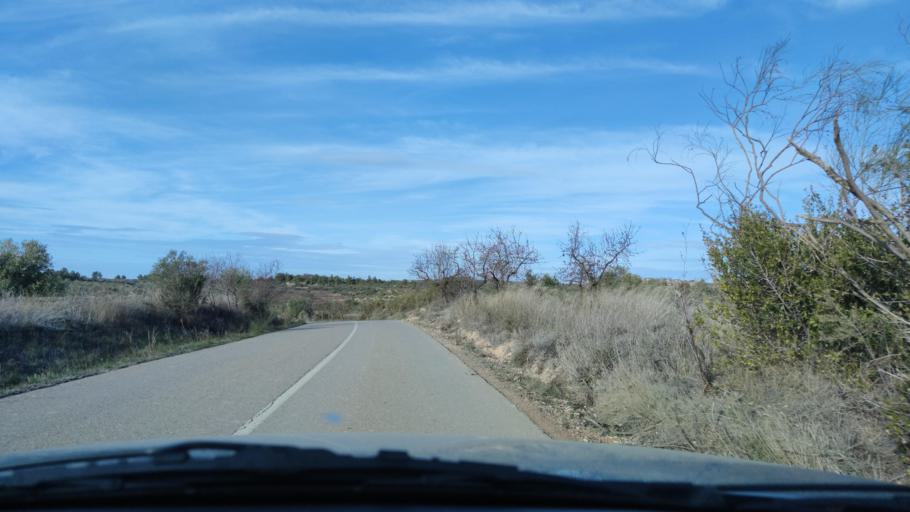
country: ES
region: Catalonia
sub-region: Provincia de Lleida
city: el Cogul
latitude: 41.4664
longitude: 0.6821
